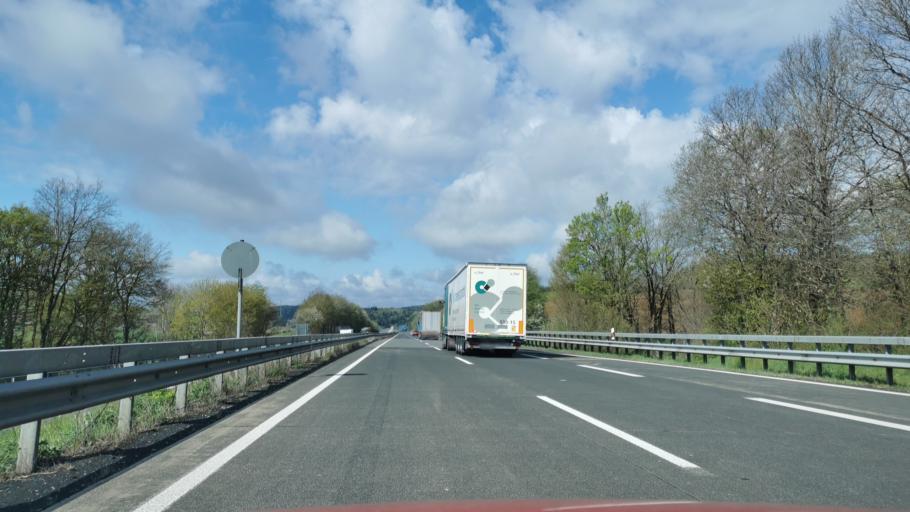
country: DE
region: Rheinland-Pfalz
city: Steiningen
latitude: 50.1923
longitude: 6.9219
